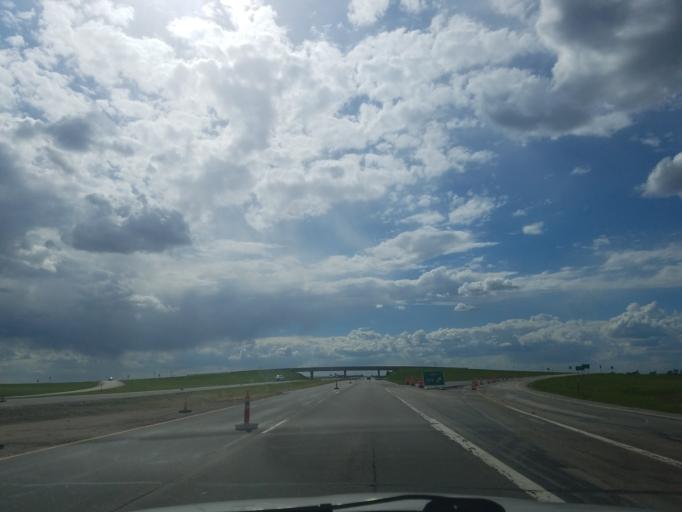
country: US
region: North Dakota
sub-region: Barnes County
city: Valley City
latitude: 46.9201
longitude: -97.7827
